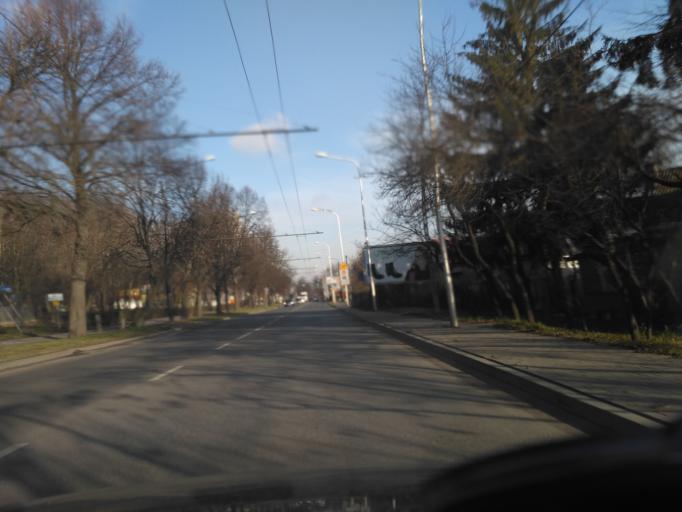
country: PL
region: Lublin Voivodeship
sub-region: Powiat lubelski
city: Lublin
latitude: 51.2102
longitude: 22.5724
